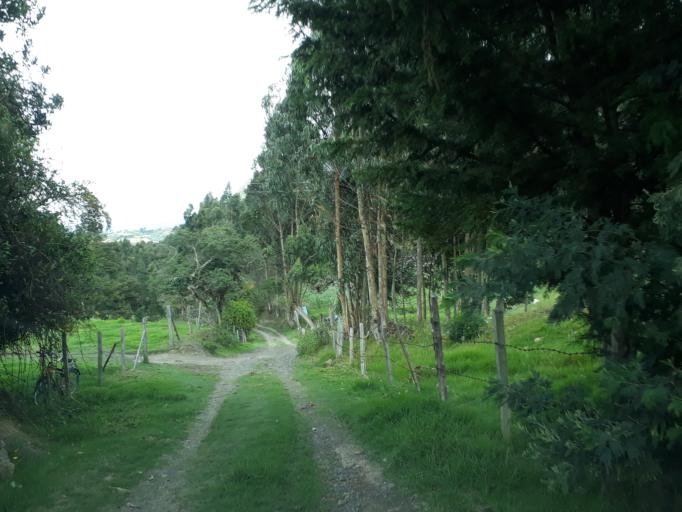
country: CO
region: Cundinamarca
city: Simijaca
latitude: 5.4787
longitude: -73.8866
